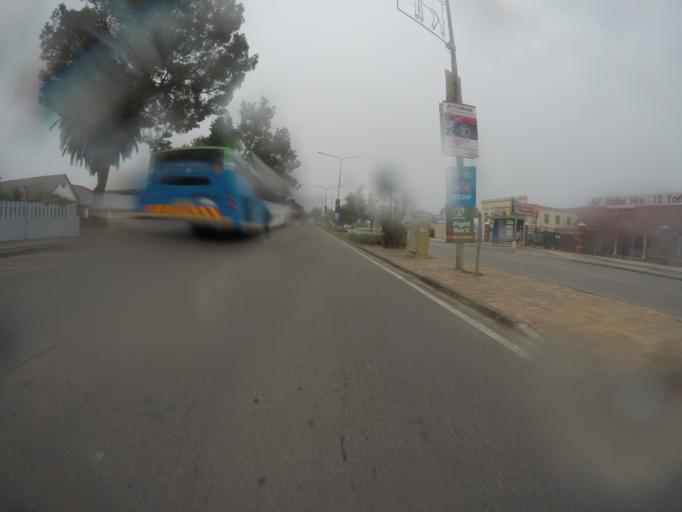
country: ZA
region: Western Cape
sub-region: Eden District Municipality
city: George
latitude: -33.9705
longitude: 22.4475
